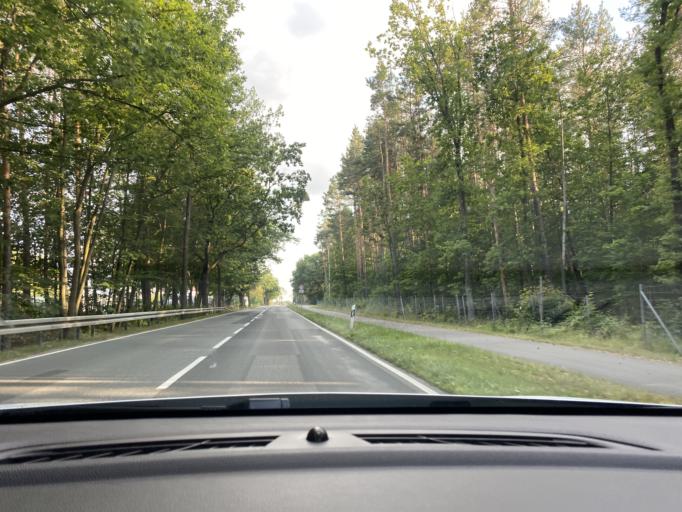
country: DE
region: Saxony
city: Konigswartha
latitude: 51.3391
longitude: 14.3422
